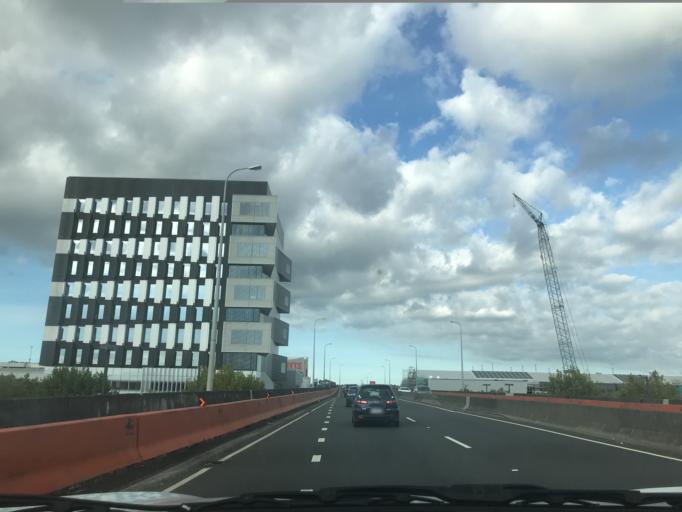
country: NZ
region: Auckland
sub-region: Auckland
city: Tamaki
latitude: -36.9158
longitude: 174.8390
